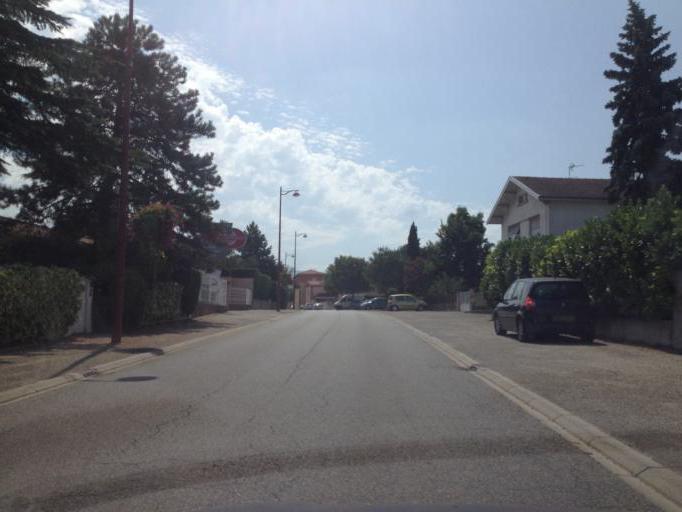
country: FR
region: Rhone-Alpes
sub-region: Departement de la Drome
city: Chatuzange-le-Goubet
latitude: 45.0087
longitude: 5.0892
